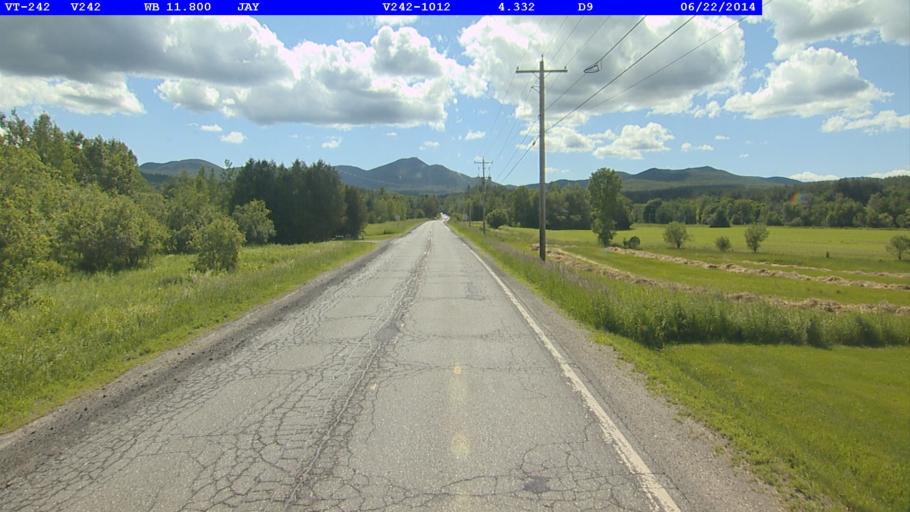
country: US
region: Vermont
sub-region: Orleans County
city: Newport
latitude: 44.9491
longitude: -72.4330
